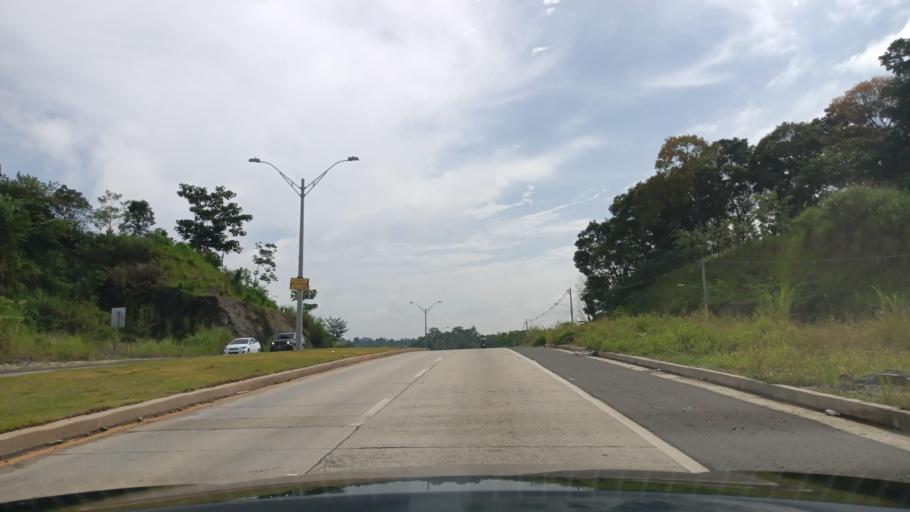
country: PA
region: Panama
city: Las Cumbres
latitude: 9.0988
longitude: -79.5121
